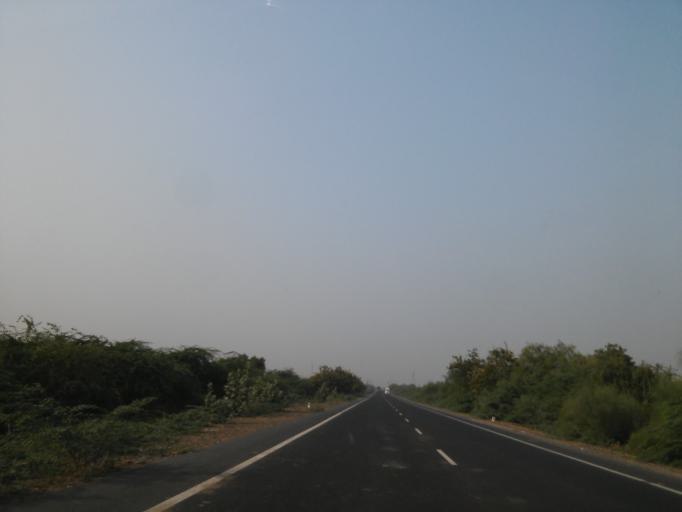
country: IN
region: Gujarat
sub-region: Kachchh
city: Anjar
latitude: 23.2841
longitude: 69.9969
